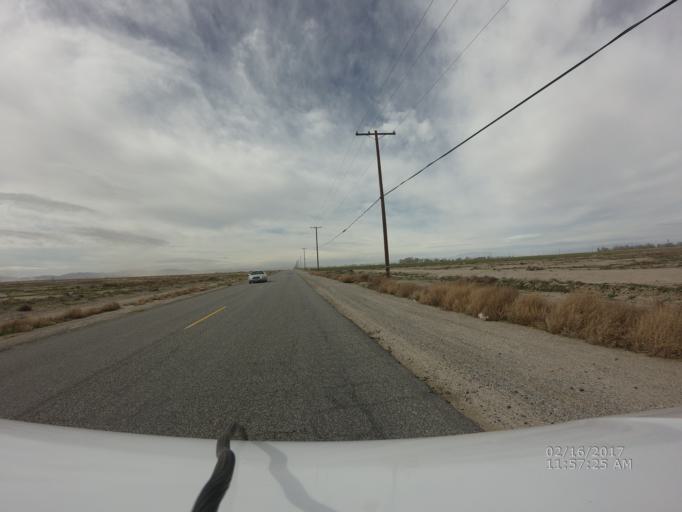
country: US
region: California
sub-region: Los Angeles County
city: Lake Los Angeles
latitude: 34.6900
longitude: -117.9150
